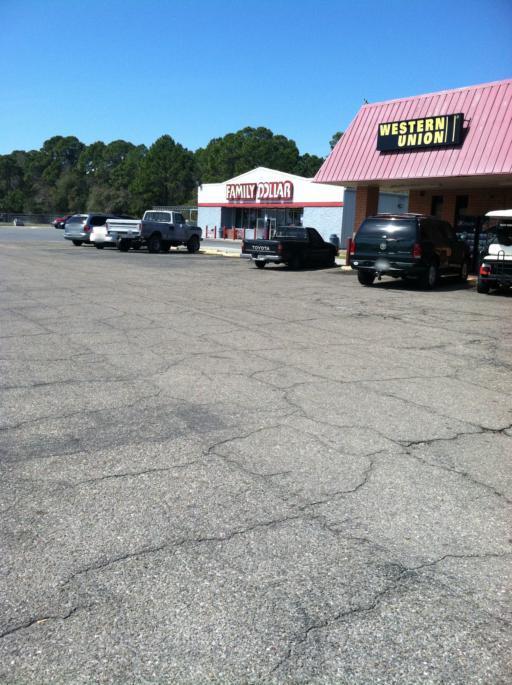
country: US
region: Florida
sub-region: Franklin County
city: Apalachicola
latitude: 29.7150
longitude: -85.0052
